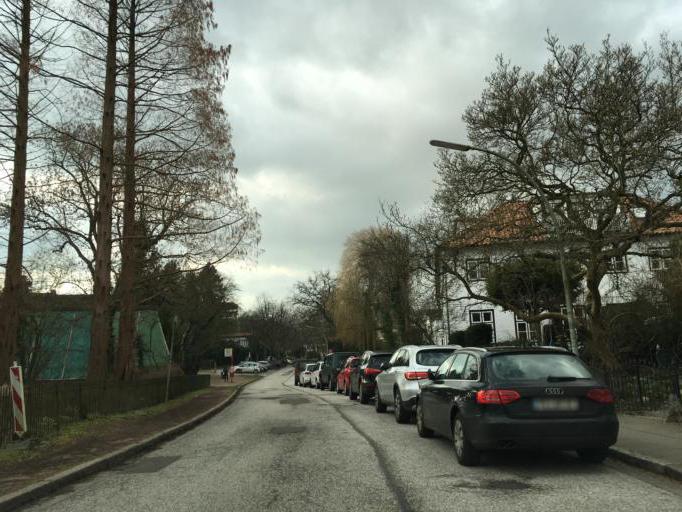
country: DE
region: Hamburg
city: Eidelstedt
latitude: 53.5550
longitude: 9.8687
